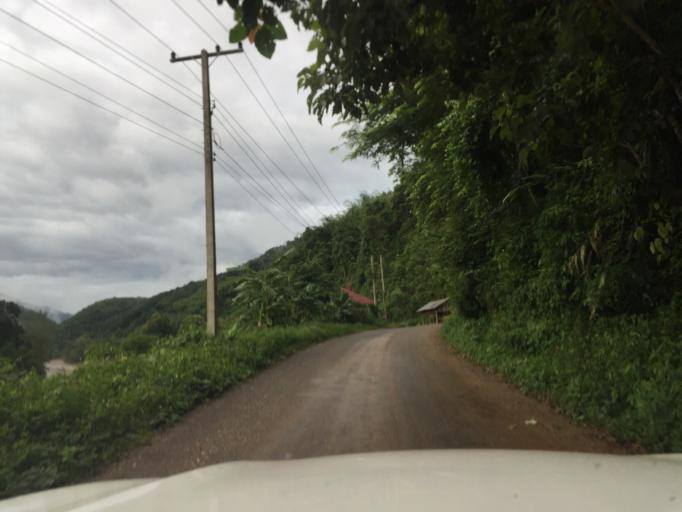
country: LA
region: Oudomxai
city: Muang La
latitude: 21.0893
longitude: 102.2427
